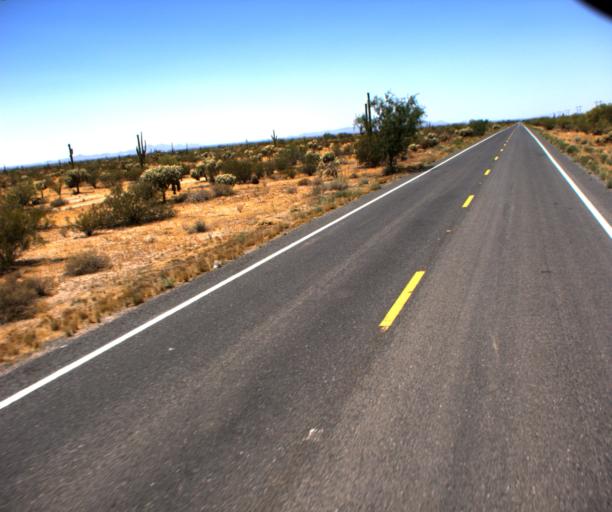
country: US
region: Arizona
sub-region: Pinal County
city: Florence
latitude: 32.8967
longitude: -111.2747
